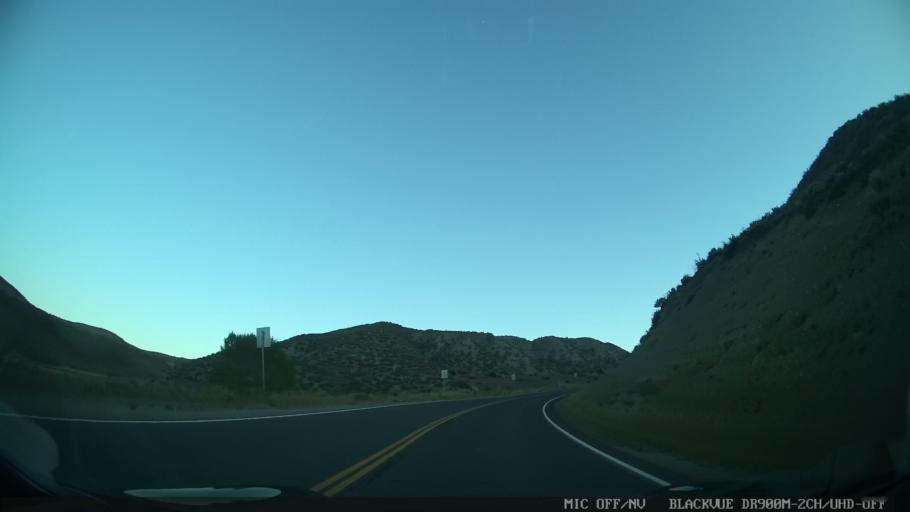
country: US
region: Colorado
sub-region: Eagle County
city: Edwards
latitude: 39.7973
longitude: -106.6799
